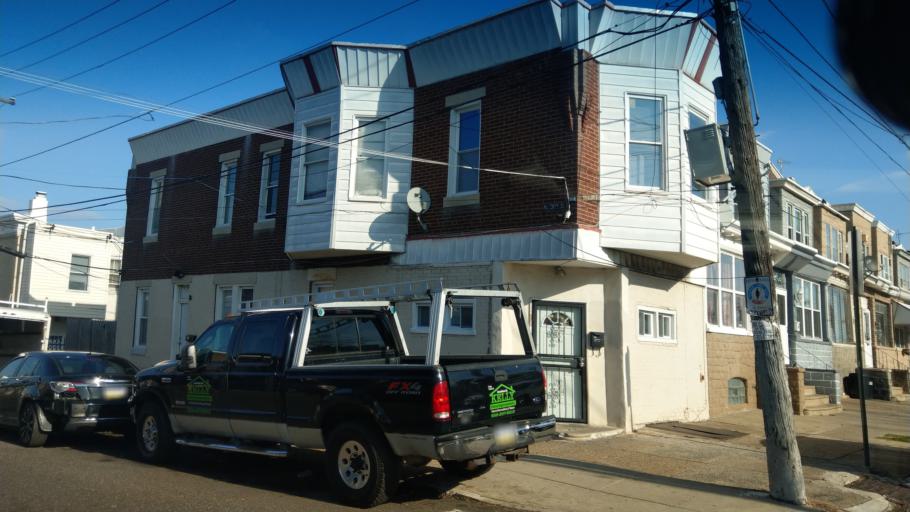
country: US
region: Pennsylvania
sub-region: Montgomery County
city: Rockledge
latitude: 40.0259
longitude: -75.1300
